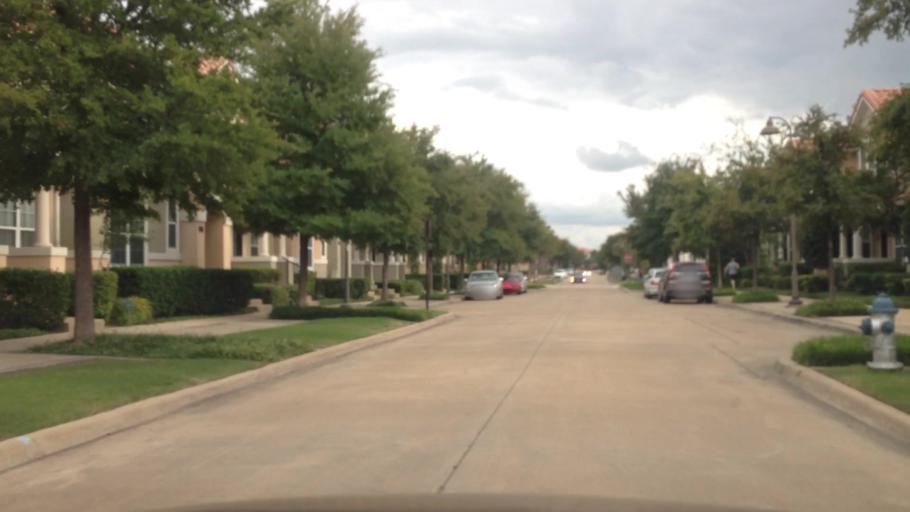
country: US
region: Texas
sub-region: Dallas County
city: Farmers Branch
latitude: 32.9022
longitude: -96.9395
